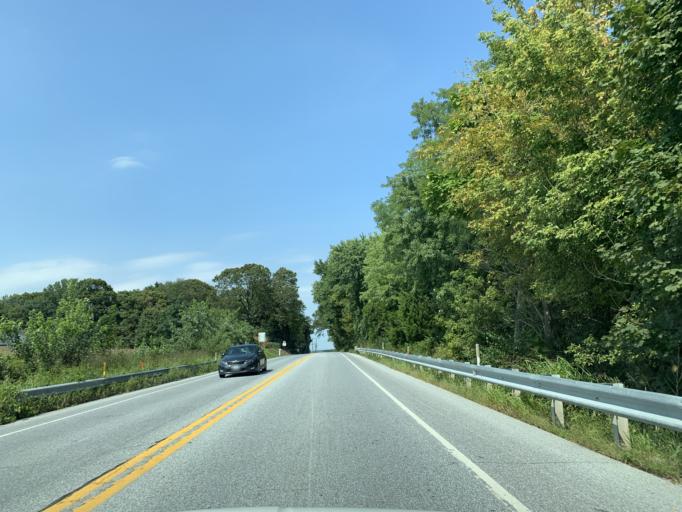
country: US
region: Pennsylvania
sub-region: York County
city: Susquehanna Trails
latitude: 39.7499
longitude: -76.3306
